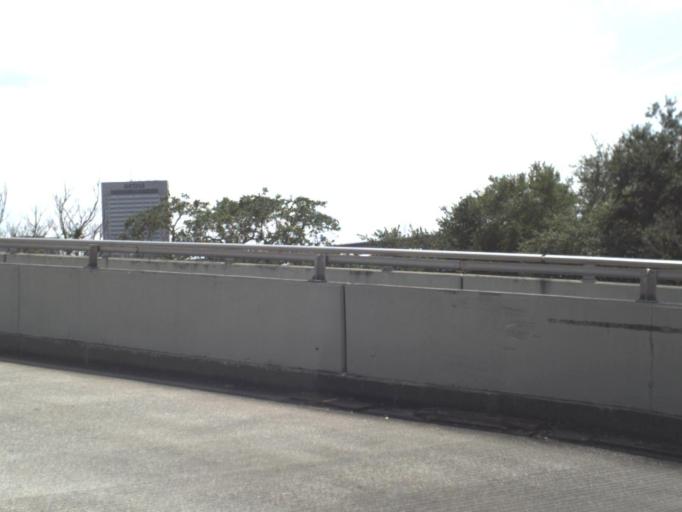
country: US
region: Florida
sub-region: Duval County
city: Jacksonville
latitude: 30.3246
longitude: -81.6585
